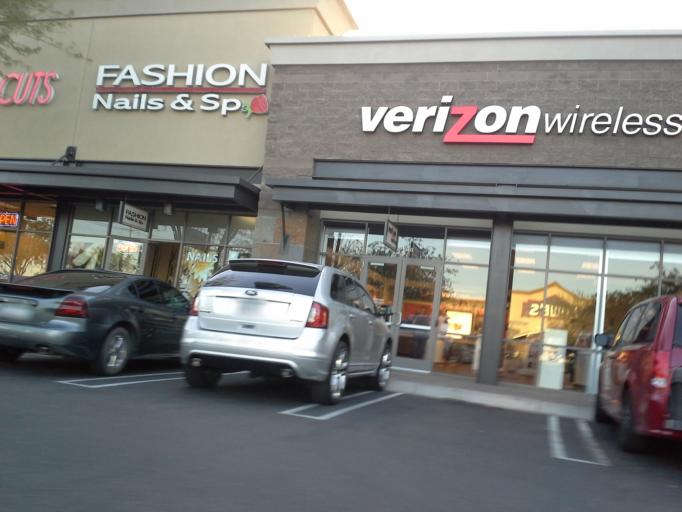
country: US
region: Arizona
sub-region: Maricopa County
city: Anthem
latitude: 33.7108
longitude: -112.1112
